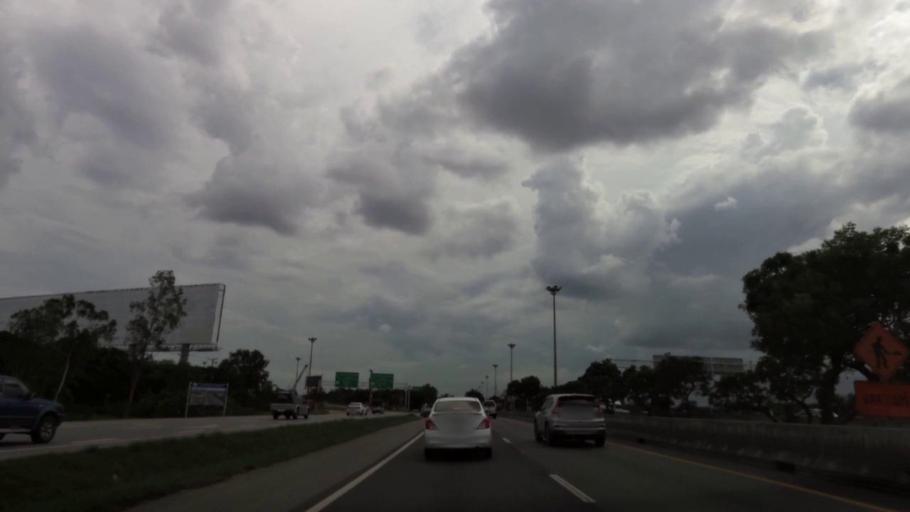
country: TH
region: Phra Nakhon Si Ayutthaya
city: Bang Pa-in
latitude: 14.1787
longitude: 100.6152
